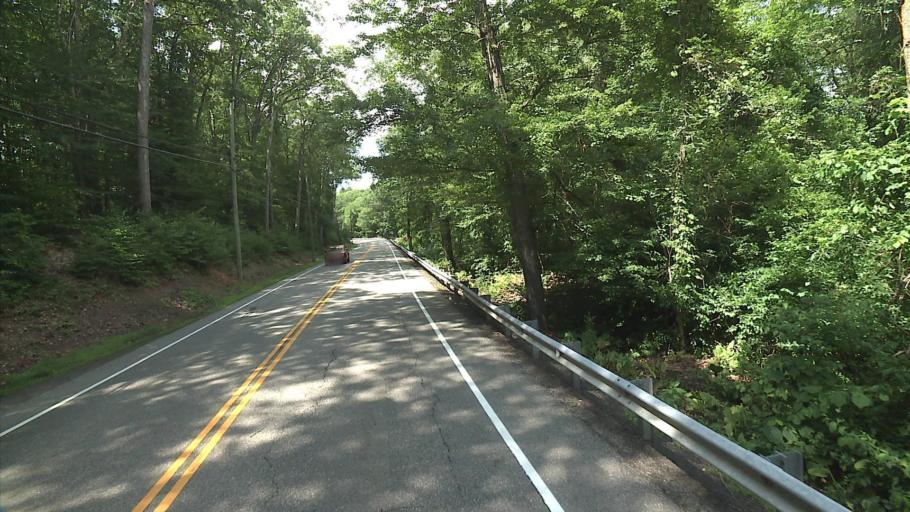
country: US
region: Connecticut
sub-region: Middlesex County
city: Clinton
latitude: 41.3334
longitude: -72.5531
